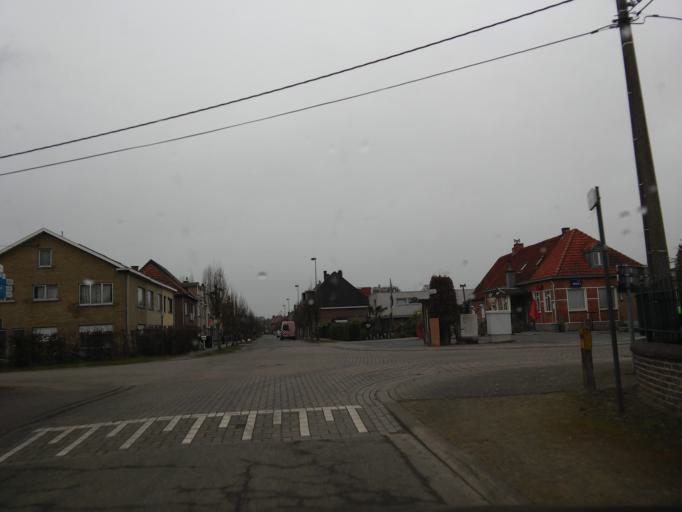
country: BE
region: Flanders
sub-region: Provincie Oost-Vlaanderen
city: Hamme
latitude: 51.0929
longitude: 4.1576
